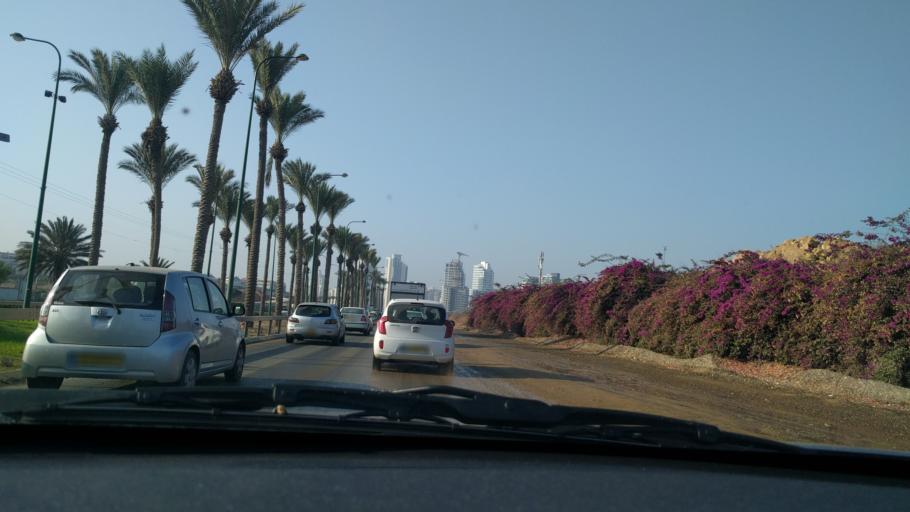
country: IL
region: Central District
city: Netanya
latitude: 32.2906
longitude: 34.8424
